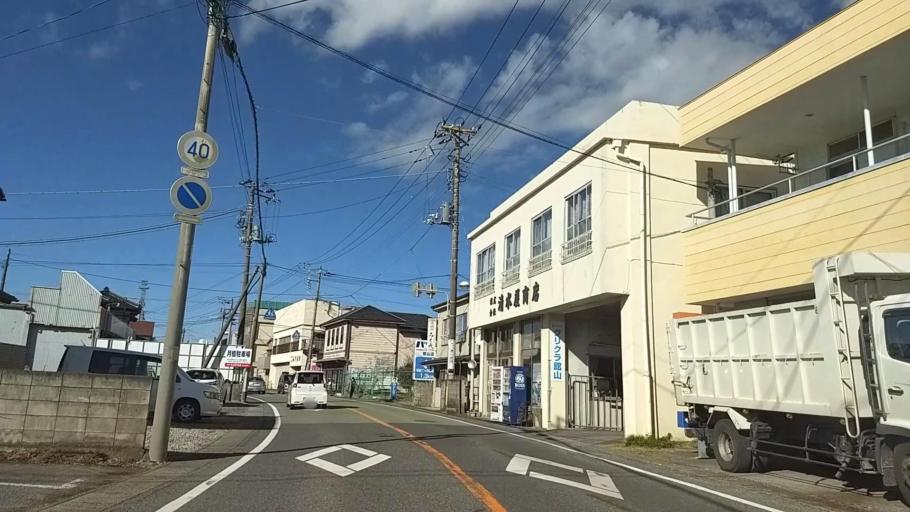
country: JP
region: Chiba
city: Tateyama
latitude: 34.9927
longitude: 139.8663
